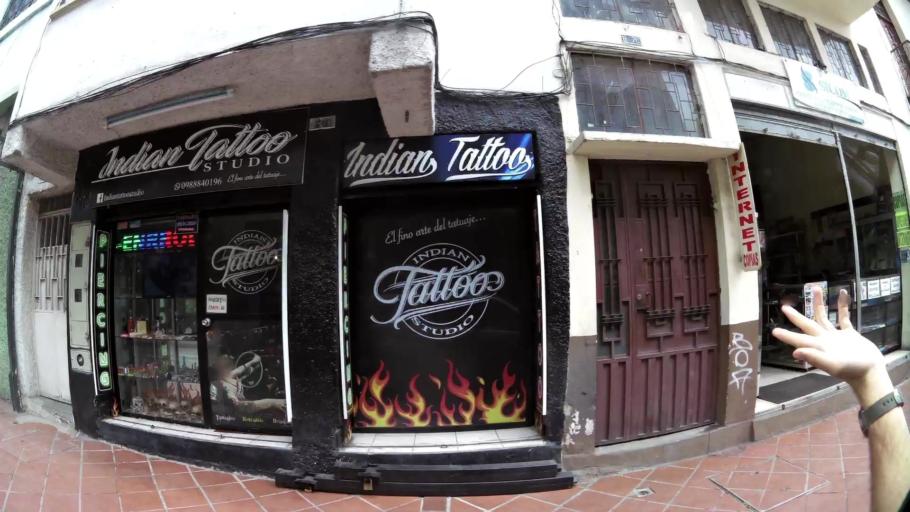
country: EC
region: Azuay
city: Cuenca
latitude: -2.8939
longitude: -79.0040
